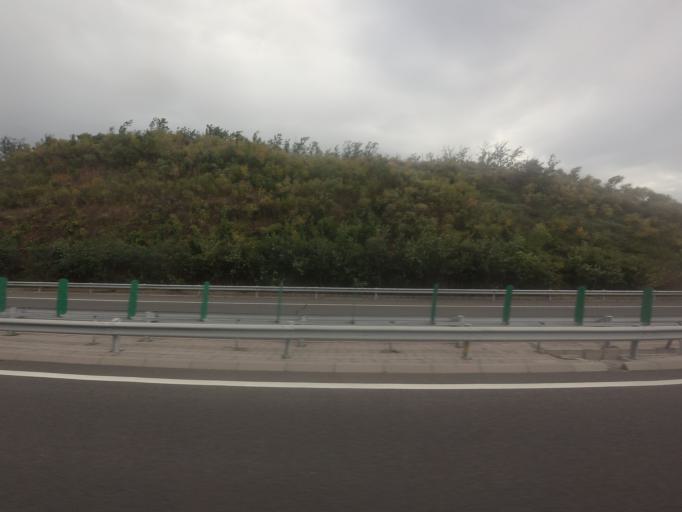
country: CN
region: Beijing
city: Dachengzi
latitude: 40.4128
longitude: 117.1328
